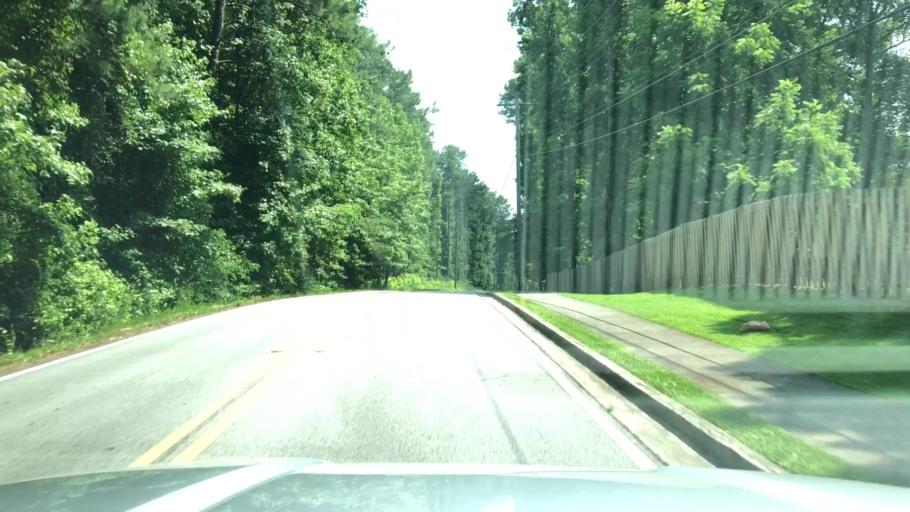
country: US
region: Georgia
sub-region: Paulding County
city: Hiram
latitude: 33.9694
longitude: -84.7247
